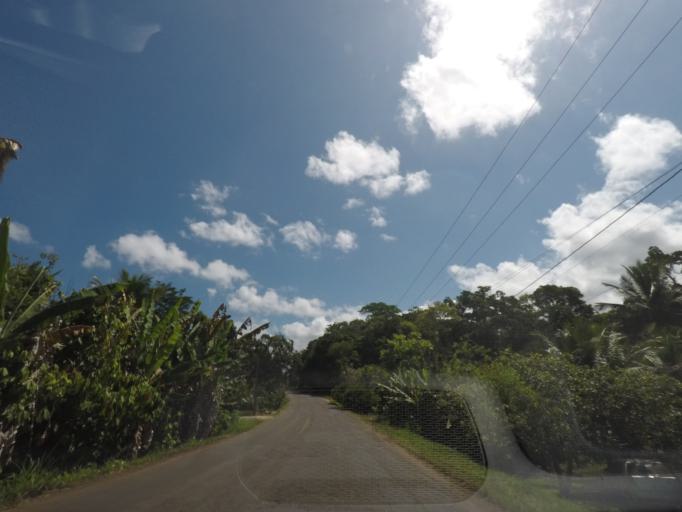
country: BR
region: Bahia
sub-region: Taperoa
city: Taperoa
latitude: -13.4973
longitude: -39.0967
